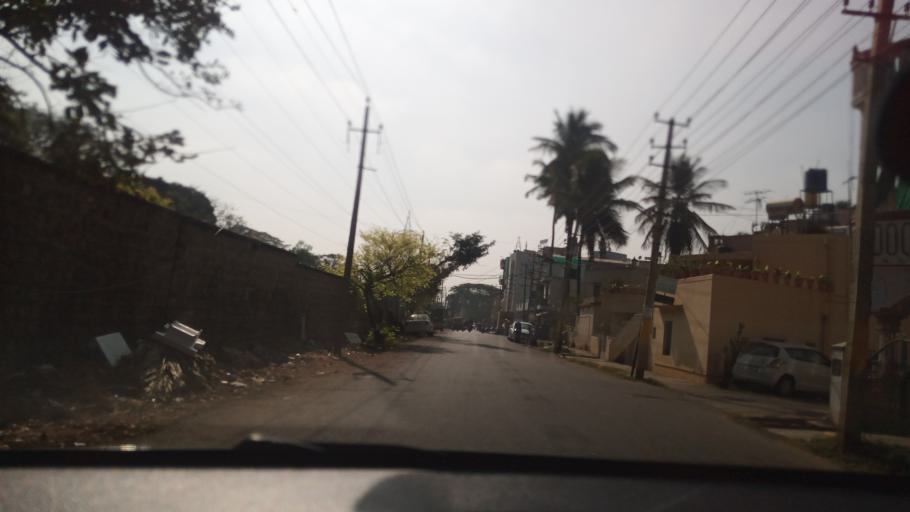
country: IN
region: Karnataka
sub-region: Bangalore Urban
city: Yelahanka
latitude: 13.0452
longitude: 77.5525
